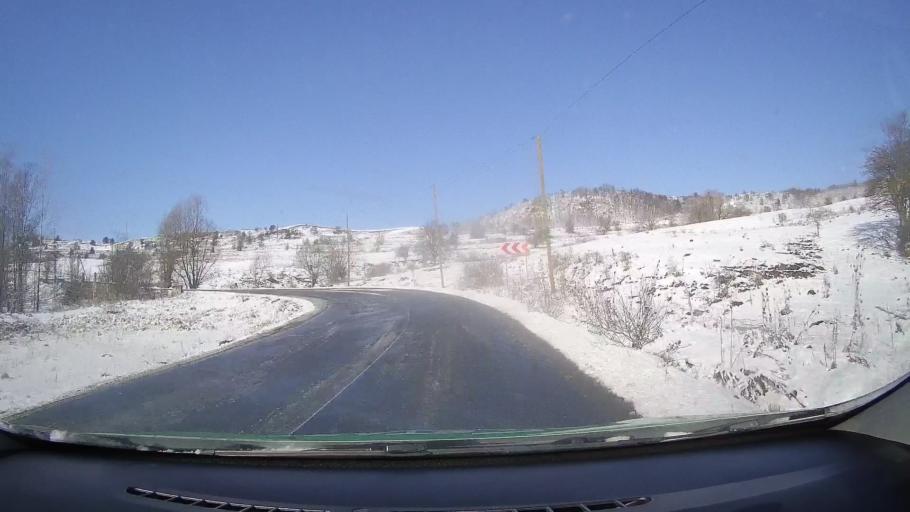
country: RO
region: Sibiu
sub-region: Comuna Avrig
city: Avrig
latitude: 45.7751
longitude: 24.3808
